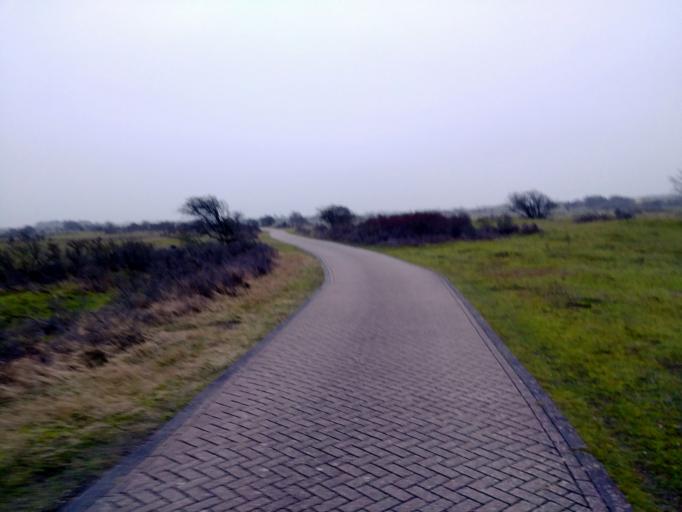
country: NL
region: South Holland
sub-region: Gemeente Noordwijkerhout
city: Noordwijkerhout
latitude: 52.3126
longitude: 4.5141
